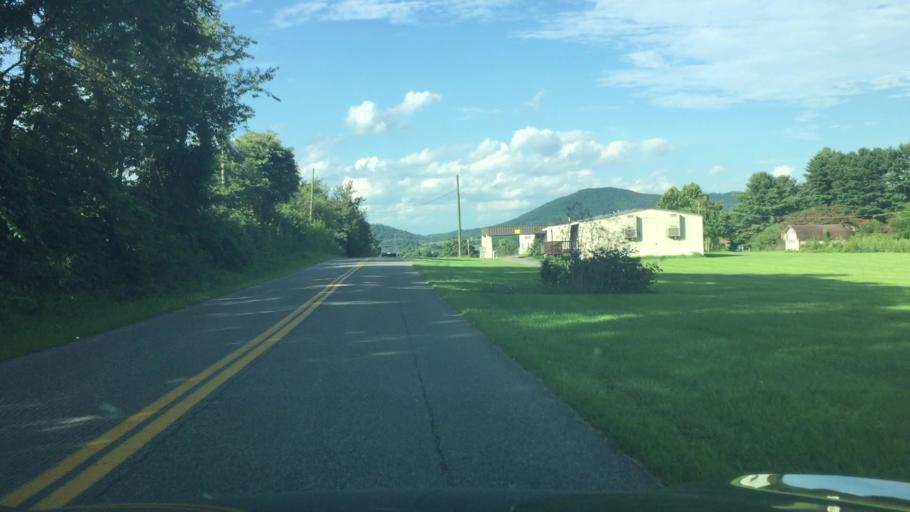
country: US
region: Virginia
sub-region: Wythe County
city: Wytheville
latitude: 36.9358
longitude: -80.9461
